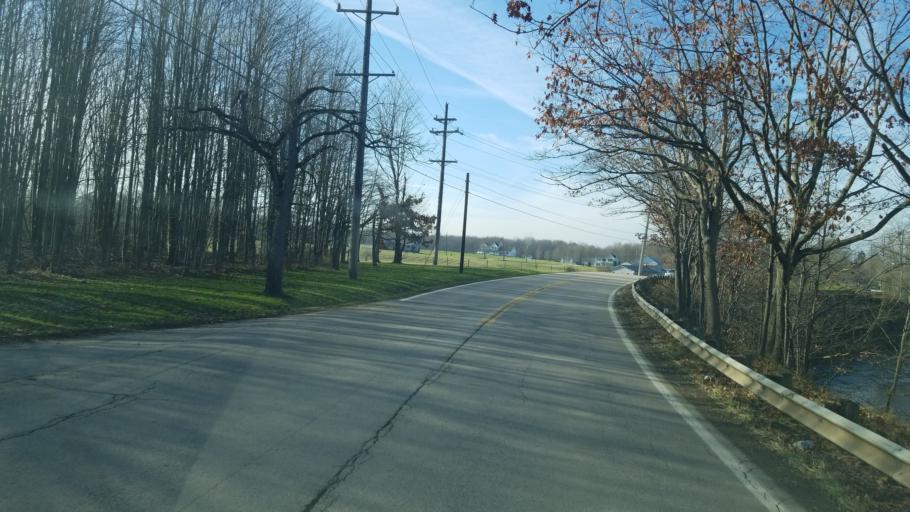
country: US
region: Ohio
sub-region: Ashtabula County
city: Jefferson
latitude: 41.7160
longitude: -80.8311
